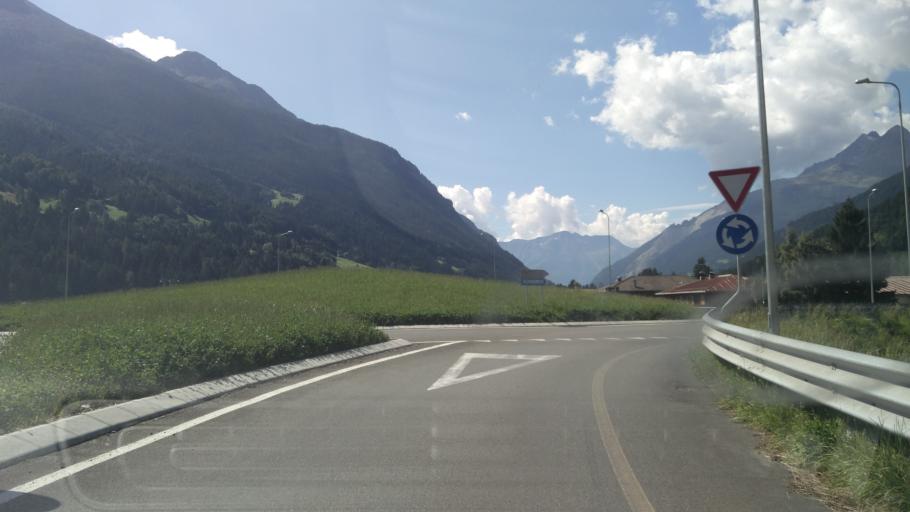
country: IT
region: Lombardy
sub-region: Provincia di Sondrio
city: Bormio
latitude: 46.4535
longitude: 10.3600
